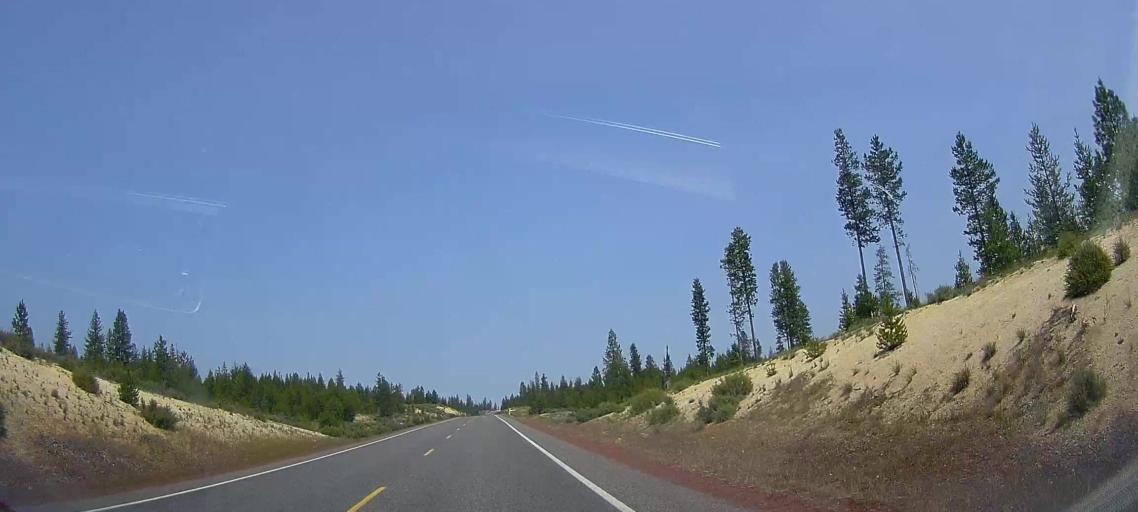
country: US
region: Oregon
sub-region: Deschutes County
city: La Pine
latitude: 43.4031
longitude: -121.7242
